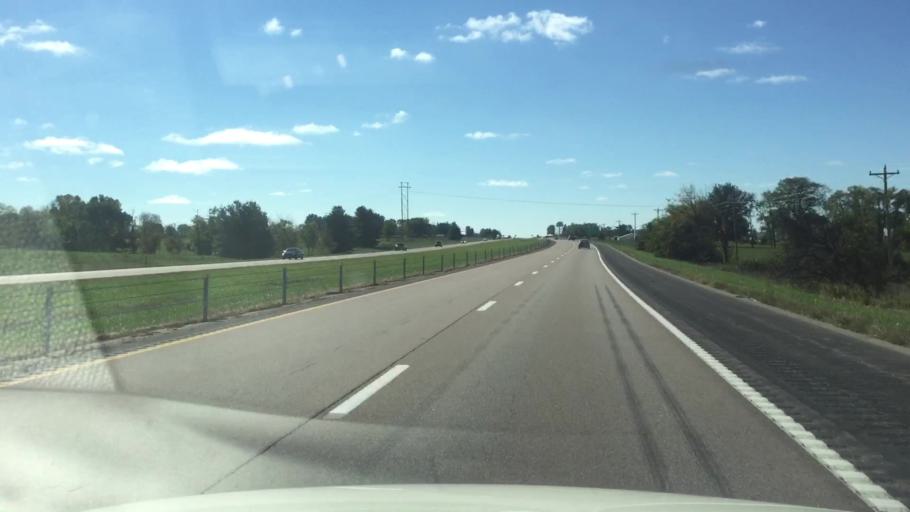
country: US
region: Missouri
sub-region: Boone County
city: Ashland
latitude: 38.7949
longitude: -92.2519
